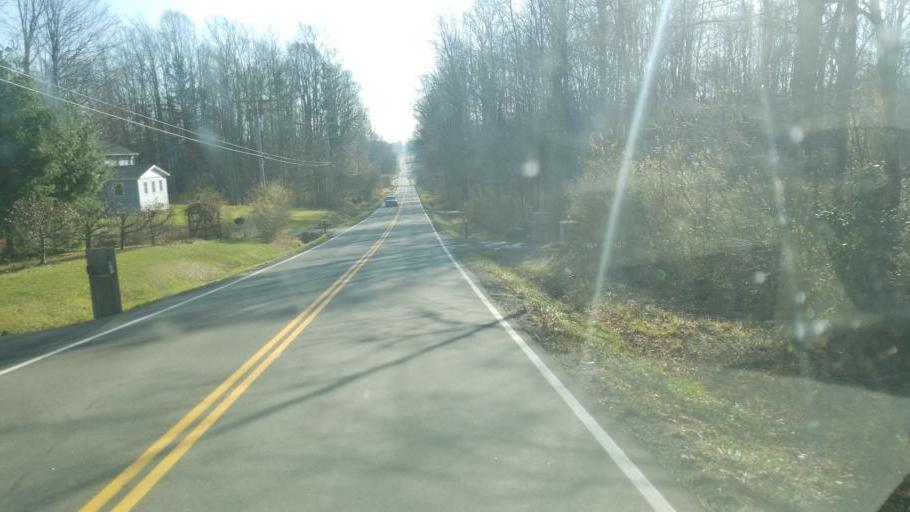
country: US
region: Ohio
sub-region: Geauga County
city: Bainbridge
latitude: 41.3753
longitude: -81.2462
